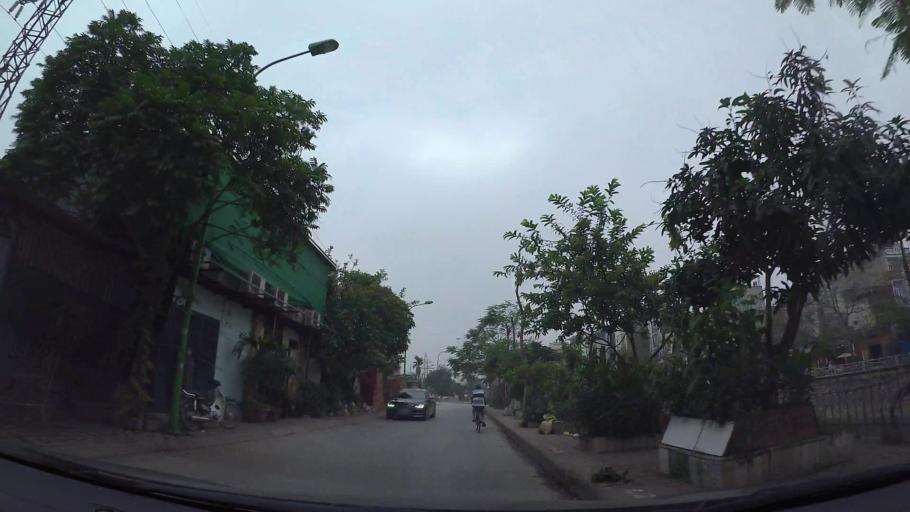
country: VN
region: Ha Noi
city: Hai BaTrung
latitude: 20.9870
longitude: 105.8446
